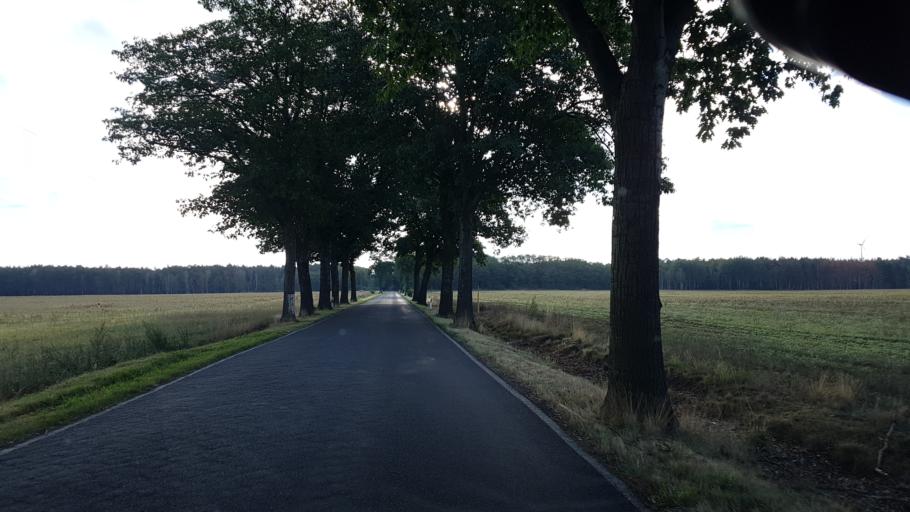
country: DE
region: Brandenburg
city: Welzow
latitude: 51.5562
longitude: 14.1468
